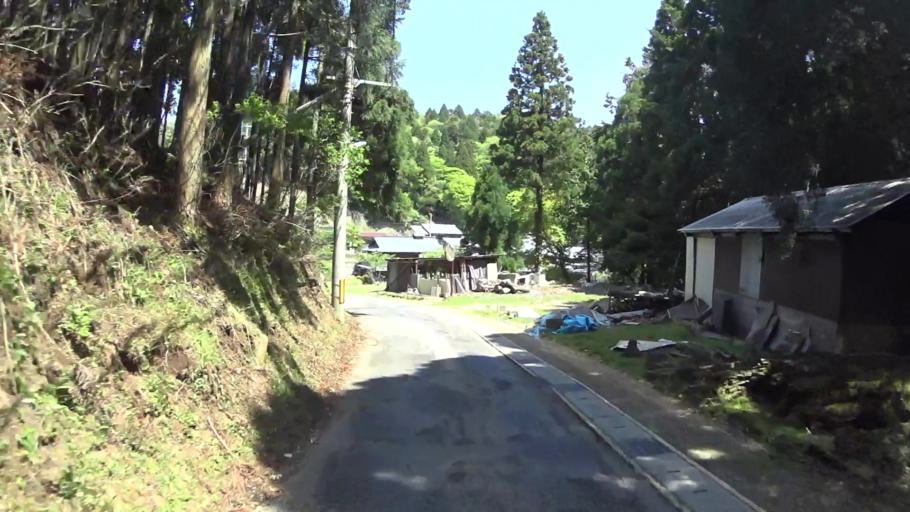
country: JP
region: Shiga Prefecture
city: Kitahama
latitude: 35.1612
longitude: 135.8100
